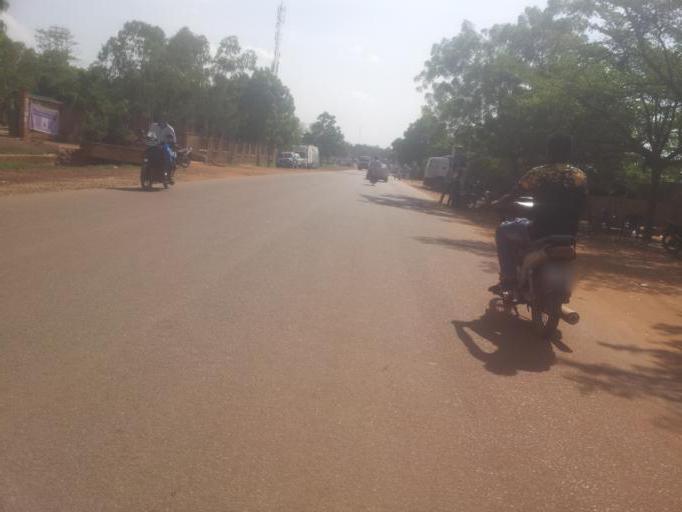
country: BF
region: Centre
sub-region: Kadiogo Province
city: Ouagadougou
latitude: 12.3645
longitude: -1.5555
